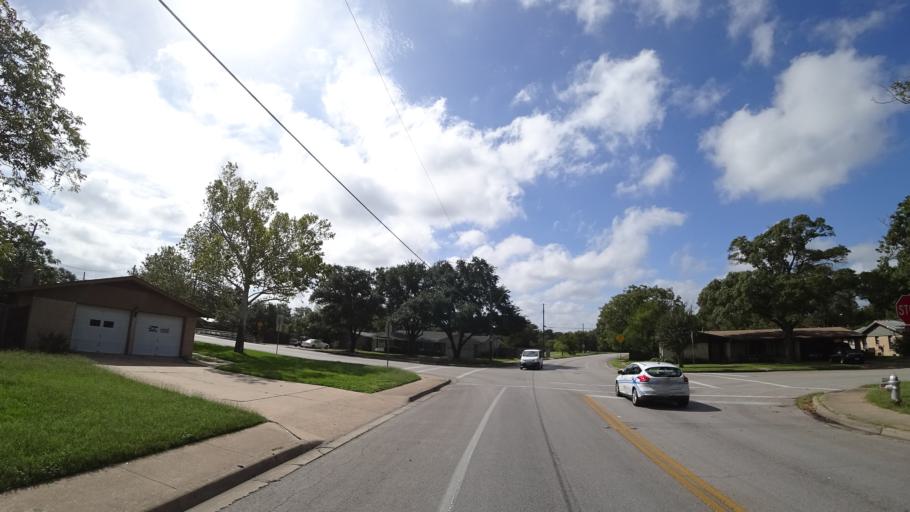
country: US
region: Texas
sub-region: Travis County
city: West Lake Hills
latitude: 30.3515
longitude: -97.7418
